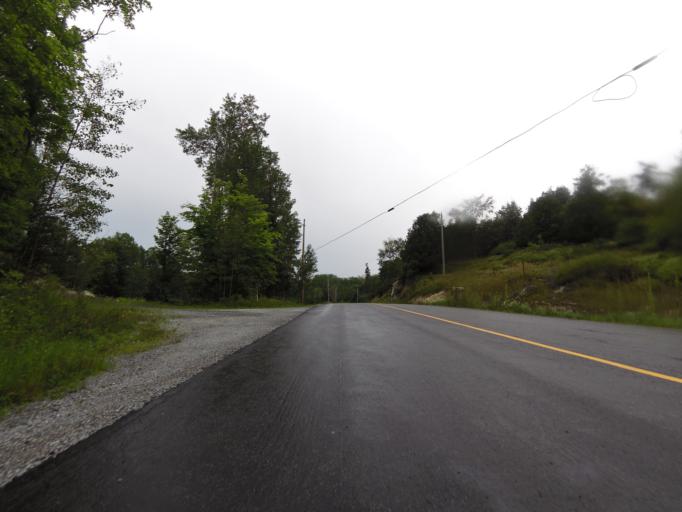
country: CA
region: Ontario
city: Perth
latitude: 44.9165
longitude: -76.4826
